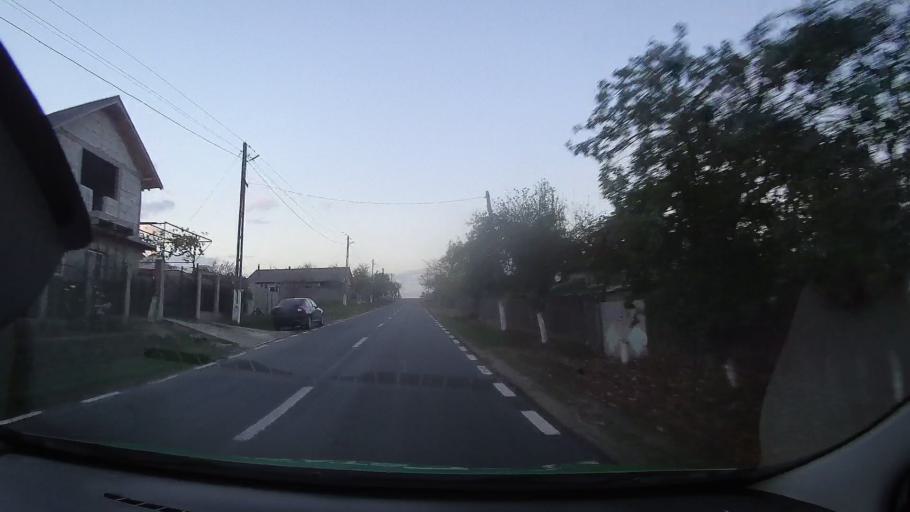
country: RO
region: Constanta
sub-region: Comuna Baneasa
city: Baneasa
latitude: 44.1010
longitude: 27.6763
